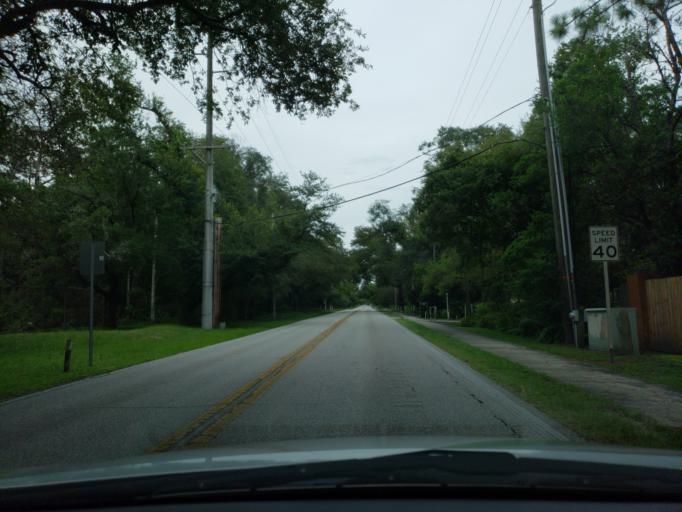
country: US
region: Florida
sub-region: Hillsborough County
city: Lutz
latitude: 28.1424
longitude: -82.4382
